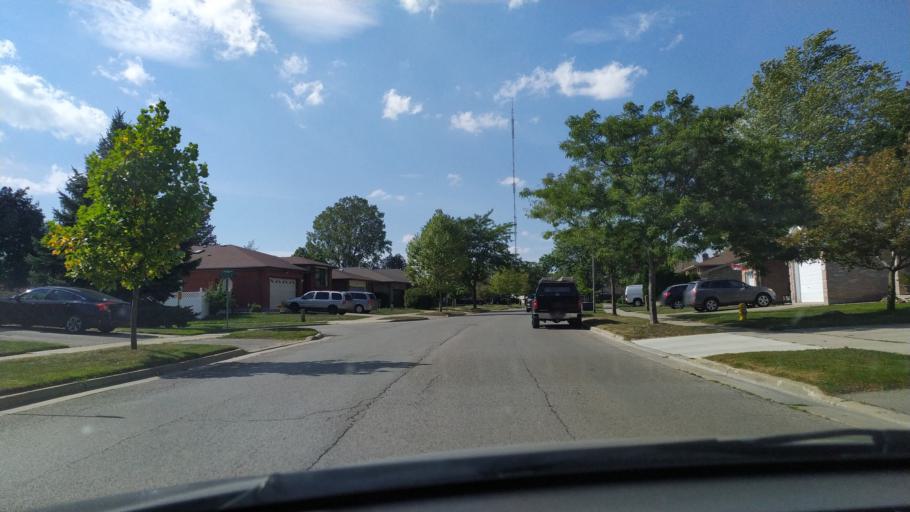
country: CA
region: Ontario
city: London
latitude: 42.9470
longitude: -81.2537
